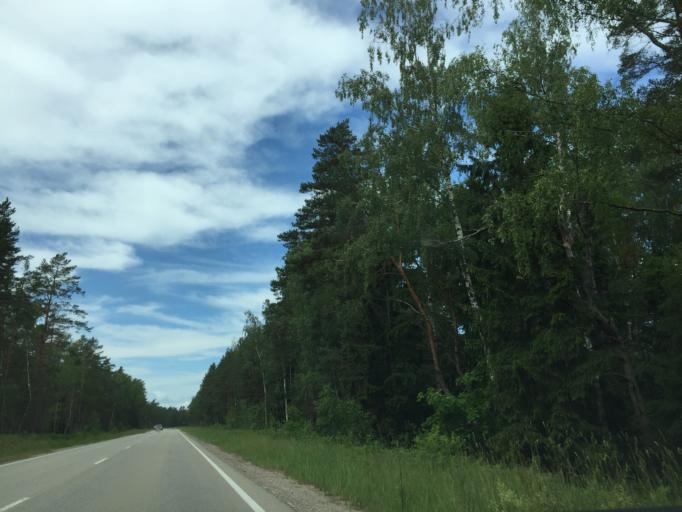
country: LV
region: Engure
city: Smarde
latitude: 57.0483
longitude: 23.3396
